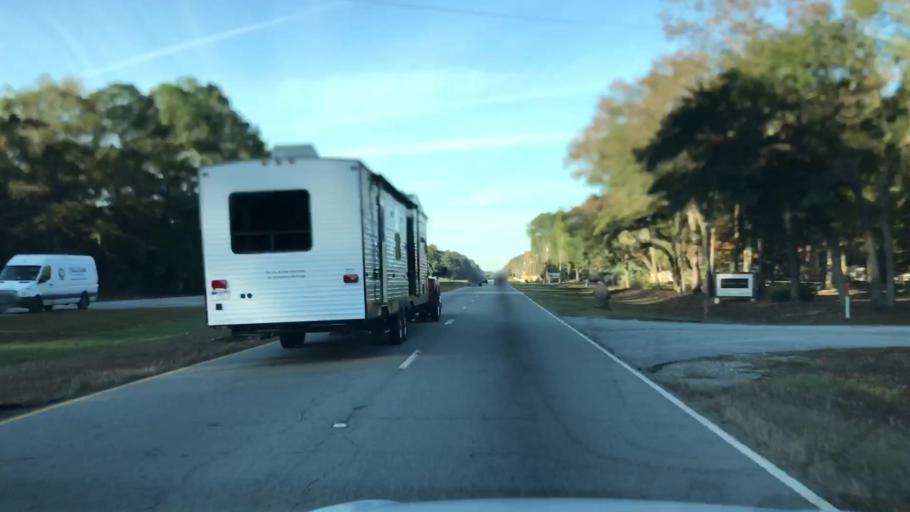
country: US
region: South Carolina
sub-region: Charleston County
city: Ravenel
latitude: 32.7747
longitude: -80.2569
